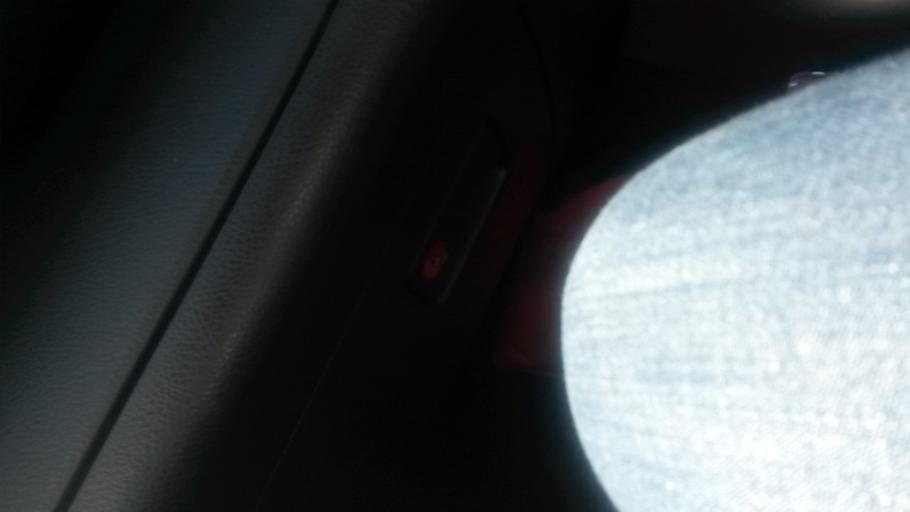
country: IE
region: Ulster
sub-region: County Donegal
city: Bundoran
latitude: 54.4837
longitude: -8.2569
